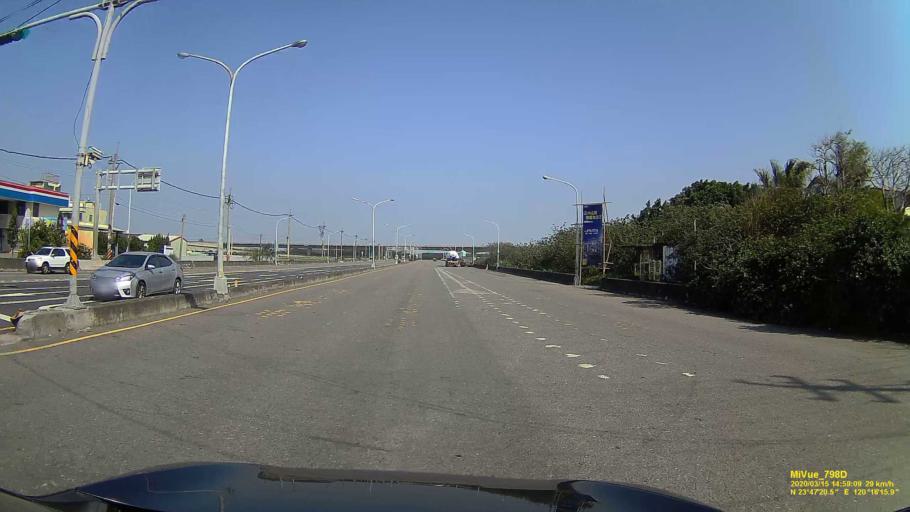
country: TW
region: Taiwan
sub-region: Yunlin
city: Douliu
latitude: 23.7890
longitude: 120.2712
